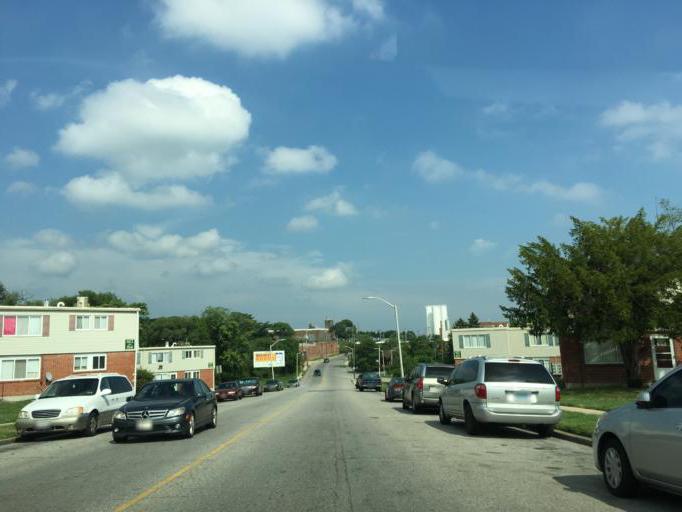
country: US
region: Maryland
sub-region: City of Baltimore
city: Baltimore
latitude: 39.3226
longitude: -76.6067
